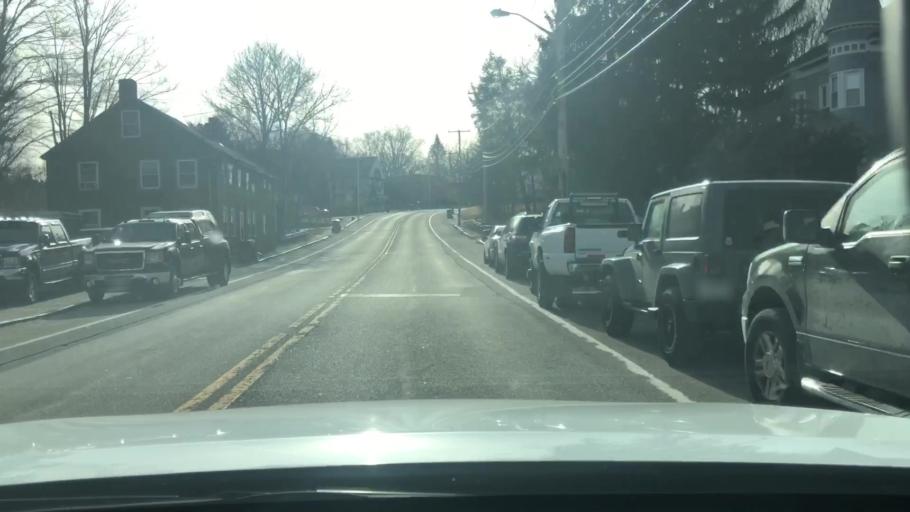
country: US
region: Massachusetts
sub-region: Worcester County
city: Upton
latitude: 42.1721
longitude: -71.6042
